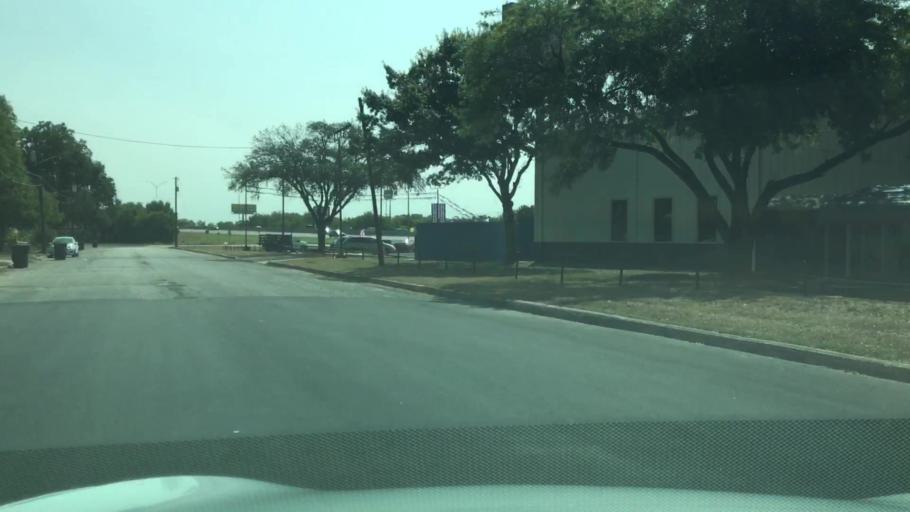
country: US
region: Texas
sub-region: Comal County
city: New Braunfels
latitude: 29.6913
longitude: -98.1140
